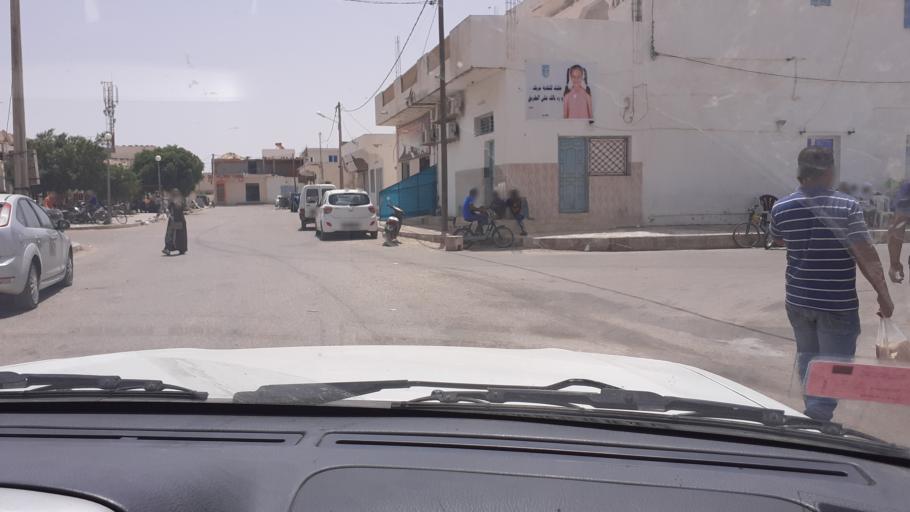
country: TN
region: Qabis
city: Matmata
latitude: 33.6175
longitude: 10.2885
